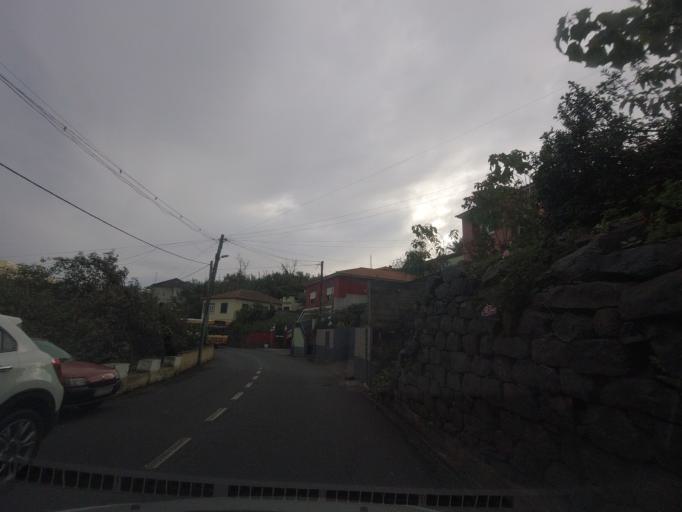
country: PT
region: Madeira
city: Camara de Lobos
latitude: 32.6686
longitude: -16.9485
